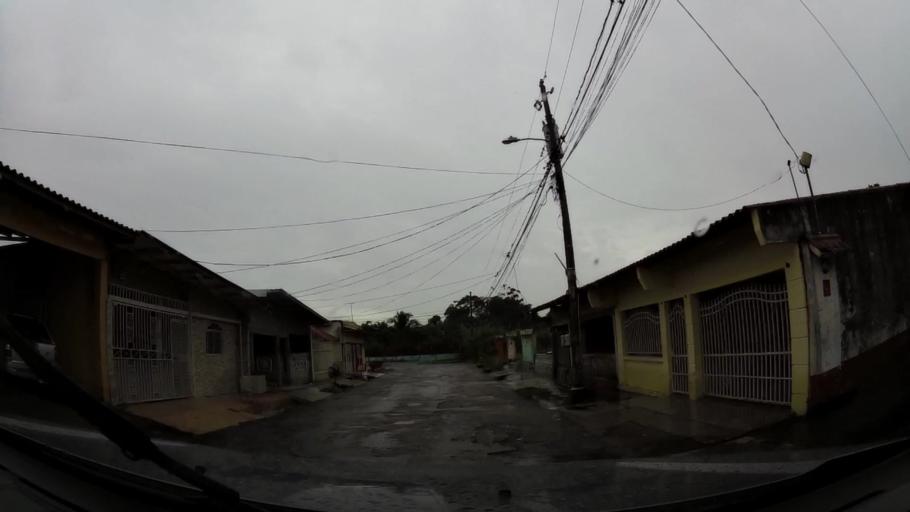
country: PA
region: Colon
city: Puerto Pilon
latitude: 9.3630
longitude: -79.8040
